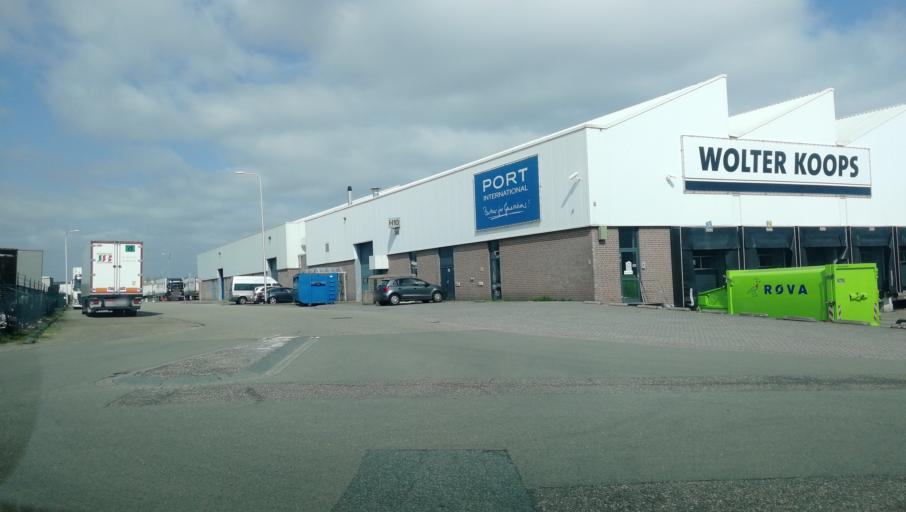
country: NL
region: Limburg
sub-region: Gemeente Venlo
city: Venlo
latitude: 51.4059
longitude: 6.1331
